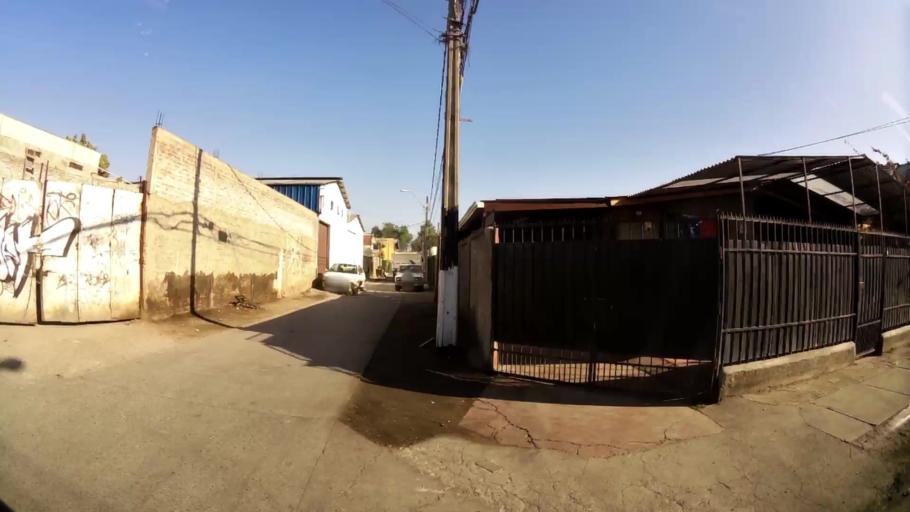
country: CL
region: Santiago Metropolitan
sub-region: Provincia de Santiago
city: Lo Prado
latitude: -33.4881
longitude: -70.7632
